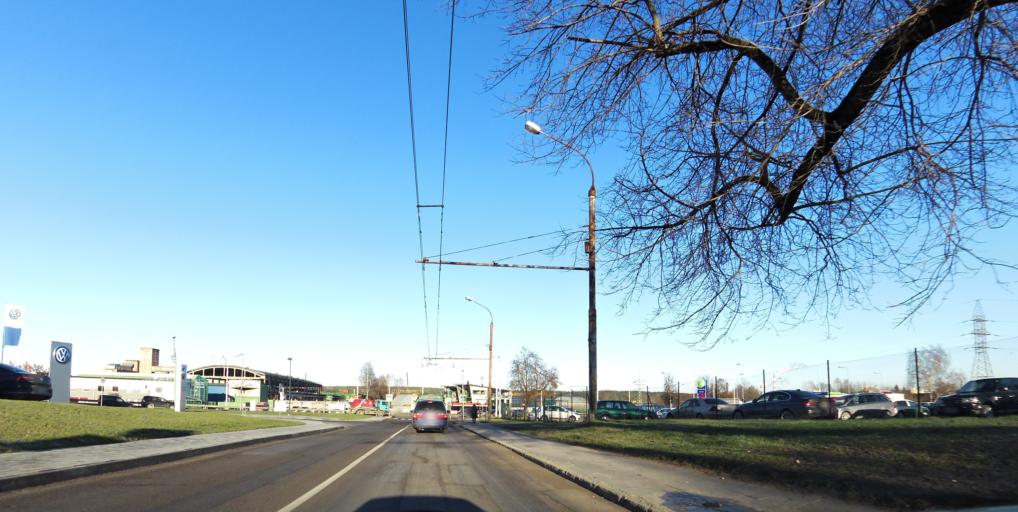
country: LT
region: Vilnius County
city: Lazdynai
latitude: 54.6432
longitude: 25.2057
